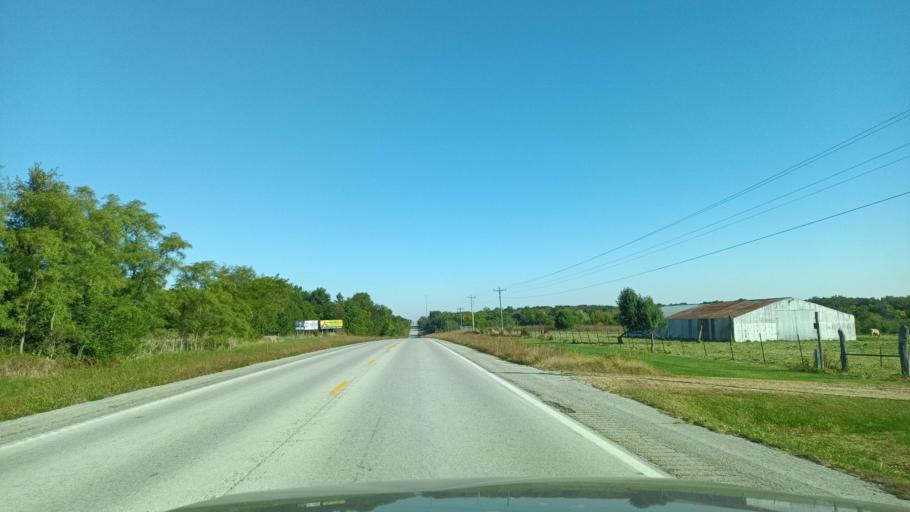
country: US
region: Missouri
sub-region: Audrain County
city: Vandalia
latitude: 39.3836
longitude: -91.6419
